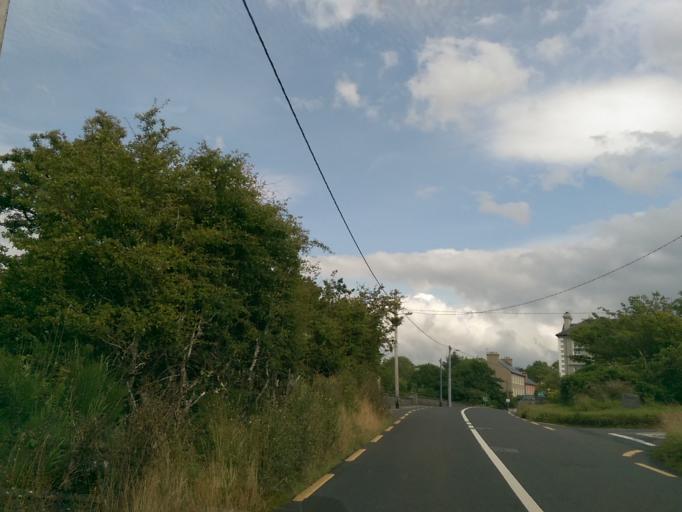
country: IE
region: Connaught
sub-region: County Galway
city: Bearna
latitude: 53.0288
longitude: -9.2973
